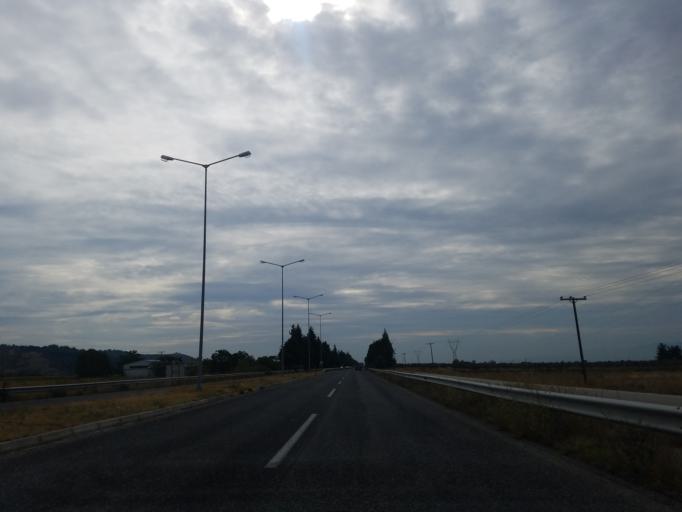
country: GR
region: Thessaly
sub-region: Trikala
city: Vasiliki
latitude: 39.6530
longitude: 21.6820
